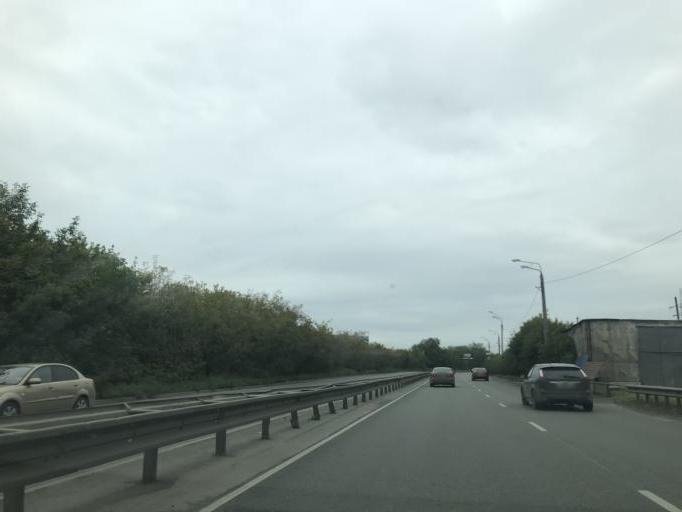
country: RU
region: Chelyabinsk
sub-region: Gorod Chelyabinsk
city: Chelyabinsk
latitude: 55.1735
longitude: 61.4250
